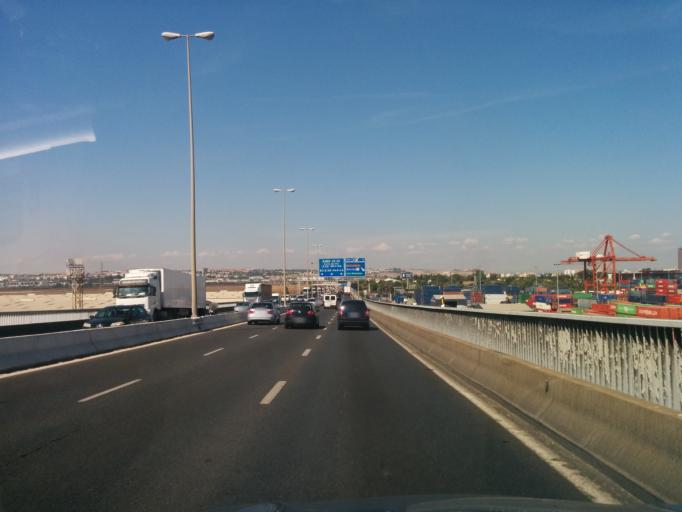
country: ES
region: Andalusia
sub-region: Provincia de Sevilla
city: Gelves
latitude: 37.3534
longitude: -5.9982
